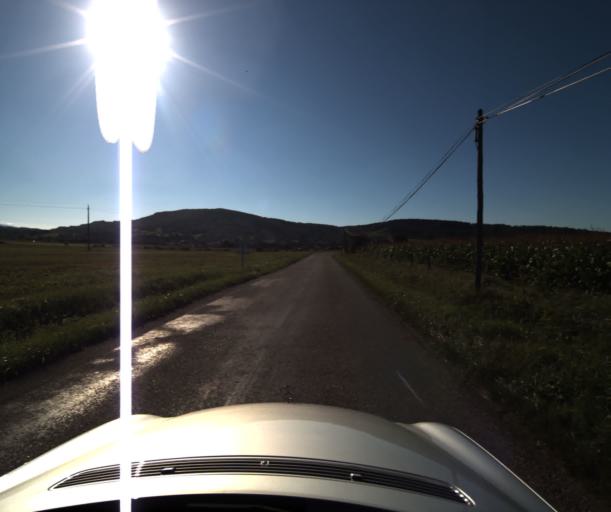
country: FR
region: Midi-Pyrenees
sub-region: Departement de l'Ariege
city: Lavelanet
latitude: 42.9930
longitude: 1.8879
